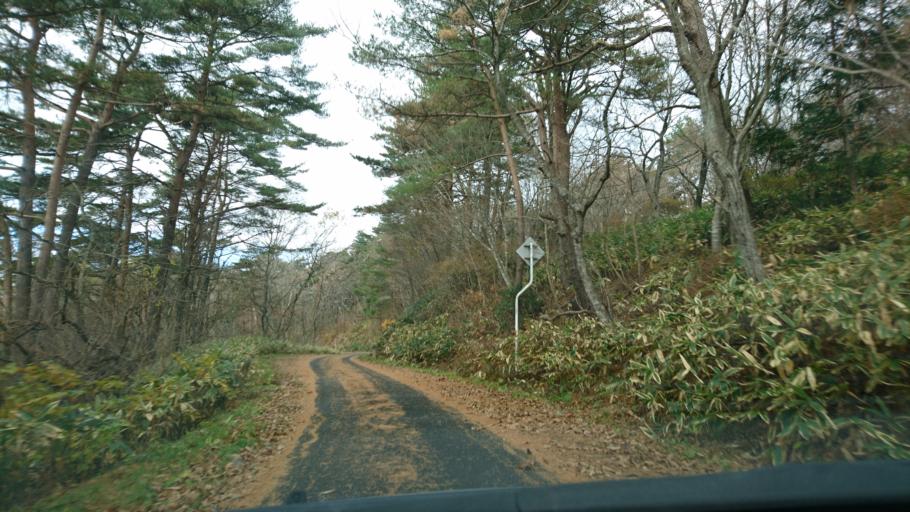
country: JP
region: Iwate
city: Ichinoseki
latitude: 39.0021
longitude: 141.1909
